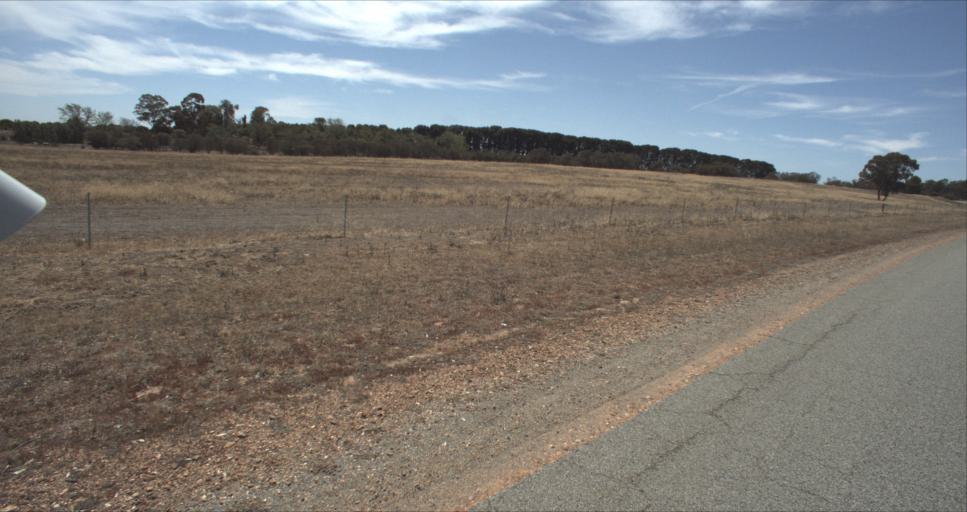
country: AU
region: New South Wales
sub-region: Leeton
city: Leeton
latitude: -34.6717
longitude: 146.4398
